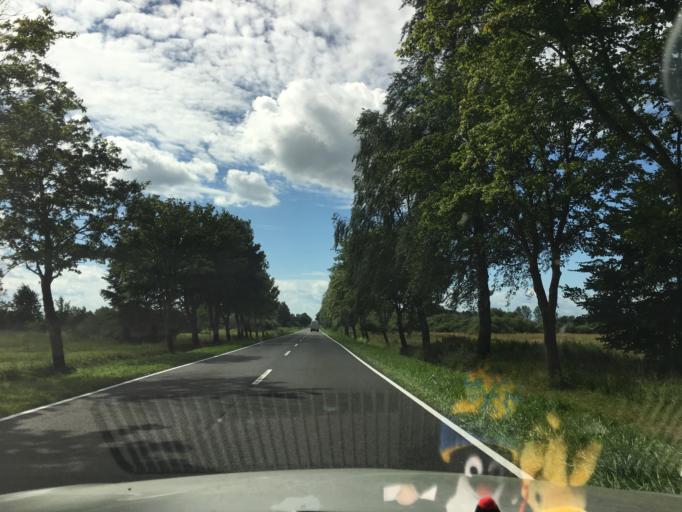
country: PL
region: West Pomeranian Voivodeship
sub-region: Powiat kamienski
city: Kamien Pomorski
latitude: 53.9291
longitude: 14.8105
